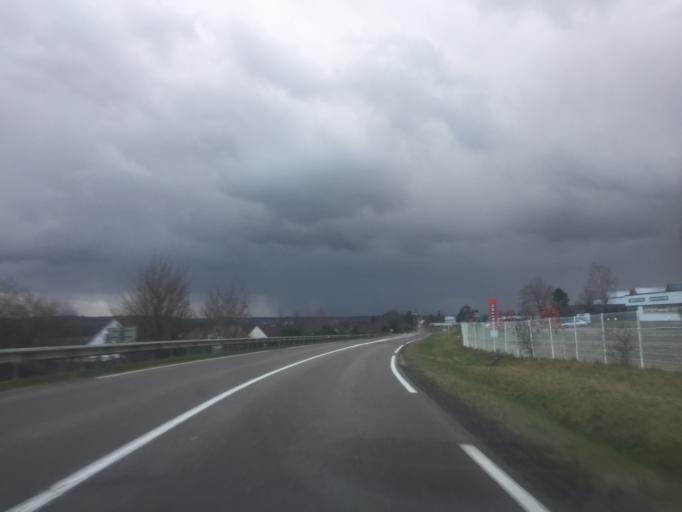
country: FR
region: Franche-Comte
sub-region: Departement du Jura
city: Fraisans
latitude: 47.1603
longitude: 5.7561
